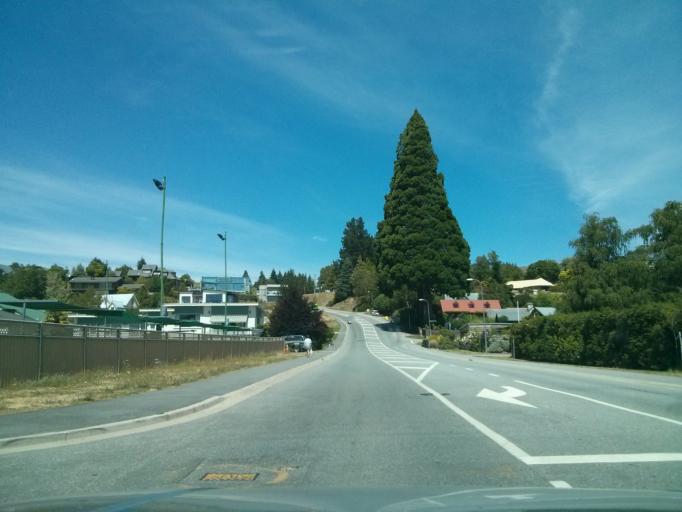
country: NZ
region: Otago
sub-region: Queenstown-Lakes District
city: Wanaka
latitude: -44.7031
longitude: 169.1321
